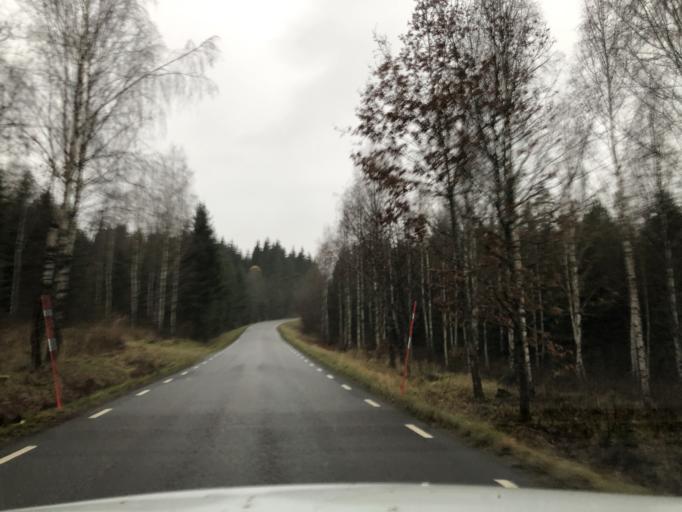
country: SE
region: Vaestra Goetaland
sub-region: Ulricehamns Kommun
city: Ulricehamn
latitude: 57.8303
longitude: 13.4107
